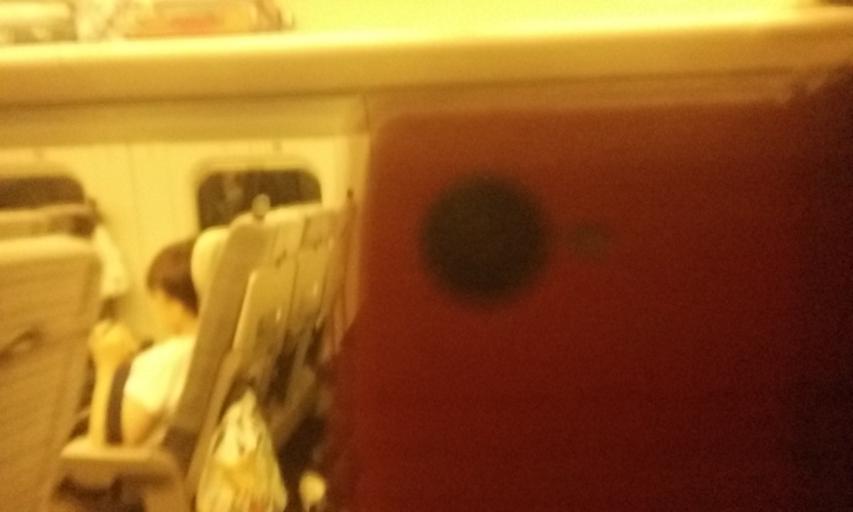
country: JP
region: Fukushima
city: Sukagawa
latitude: 37.2181
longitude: 140.2780
